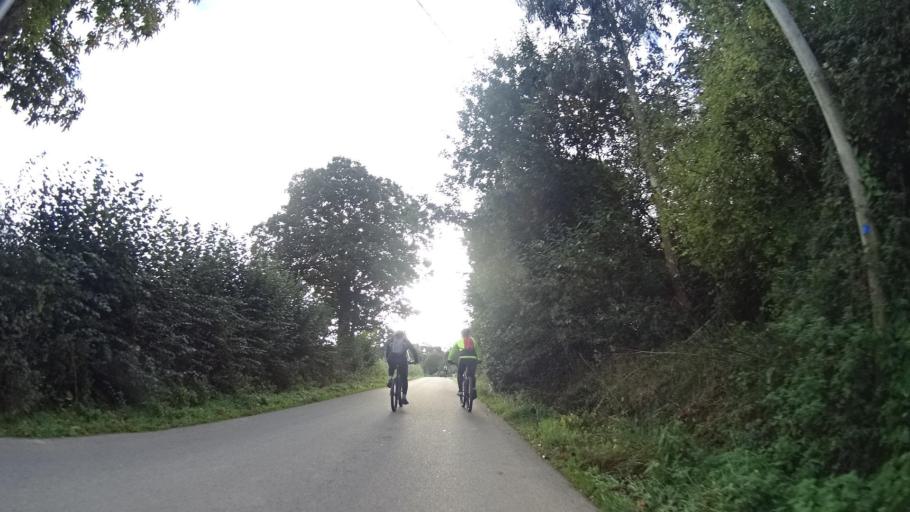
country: FR
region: Brittany
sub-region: Departement des Cotes-d'Armor
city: Evran
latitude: 48.3727
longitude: -1.9645
